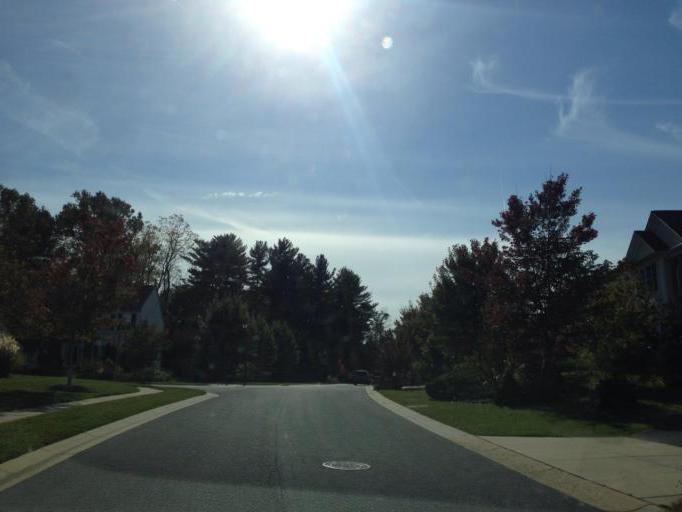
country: US
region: Maryland
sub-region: Howard County
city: Ellicott City
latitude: 39.2500
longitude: -76.8016
